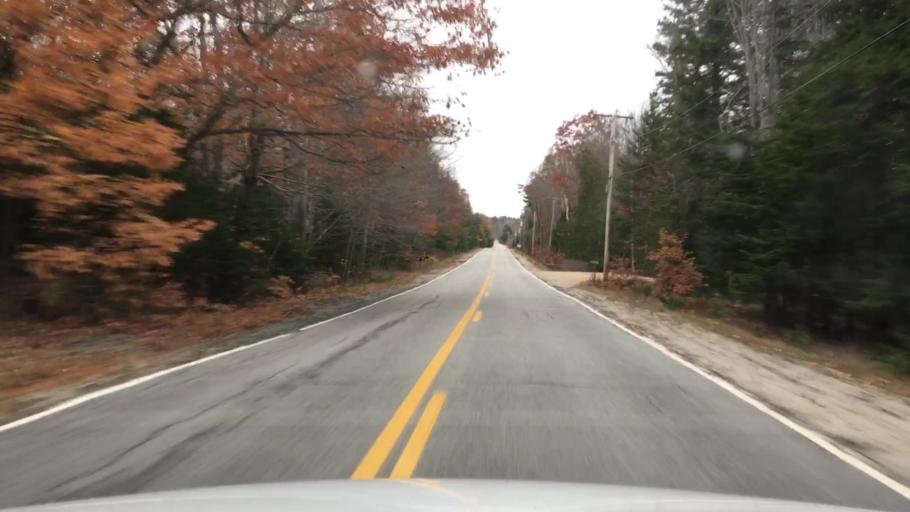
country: US
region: Maine
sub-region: Hancock County
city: Sedgwick
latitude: 44.3101
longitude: -68.5707
